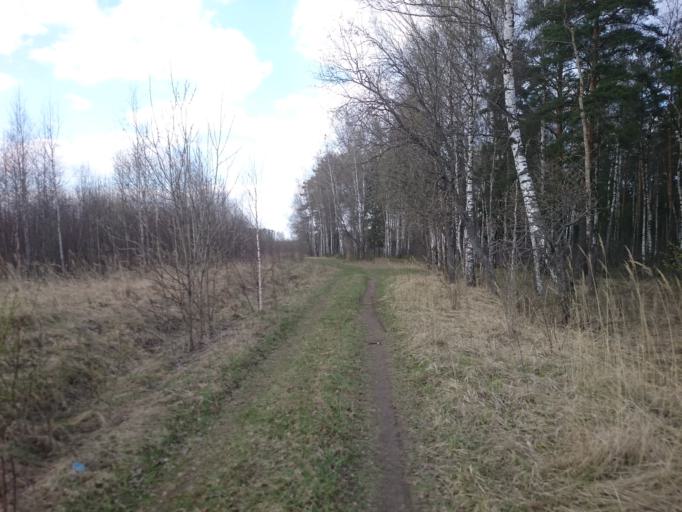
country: RU
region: Moskovskaya
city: Klin
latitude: 56.3983
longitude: 36.6815
